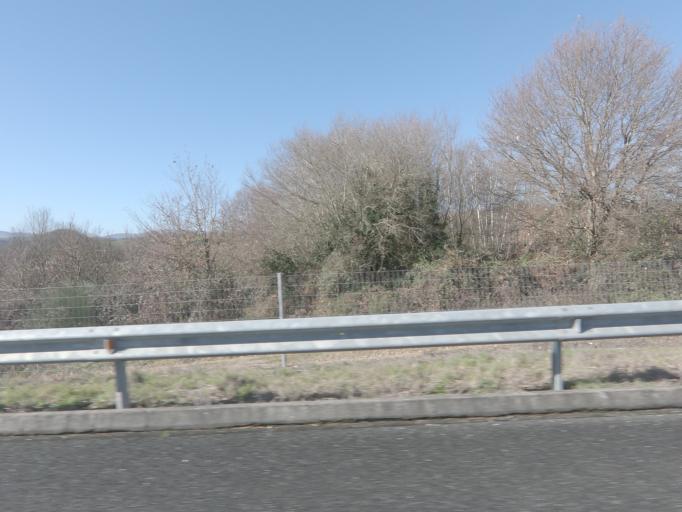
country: ES
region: Galicia
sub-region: Provincia de Pontevedra
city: Lalin
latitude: 42.6450
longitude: -8.1326
